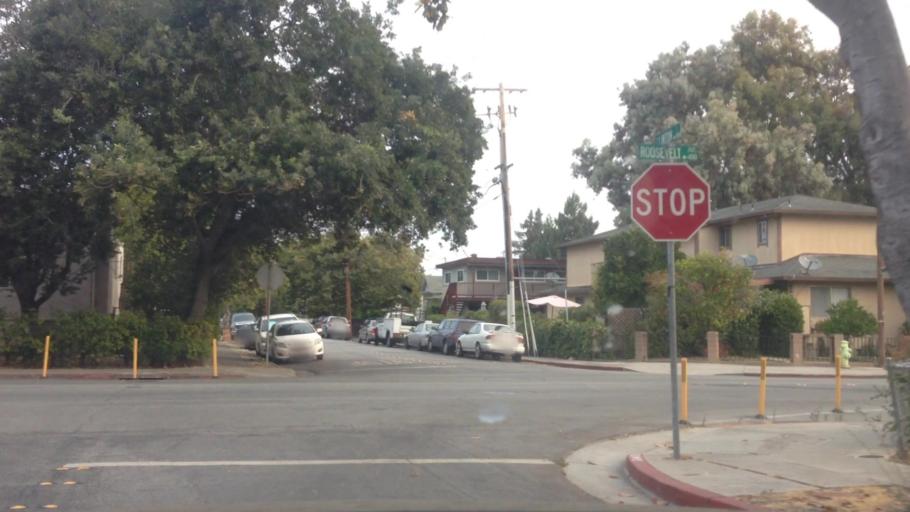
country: US
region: California
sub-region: San Mateo County
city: Redwood City
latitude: 37.4770
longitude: -122.2279
